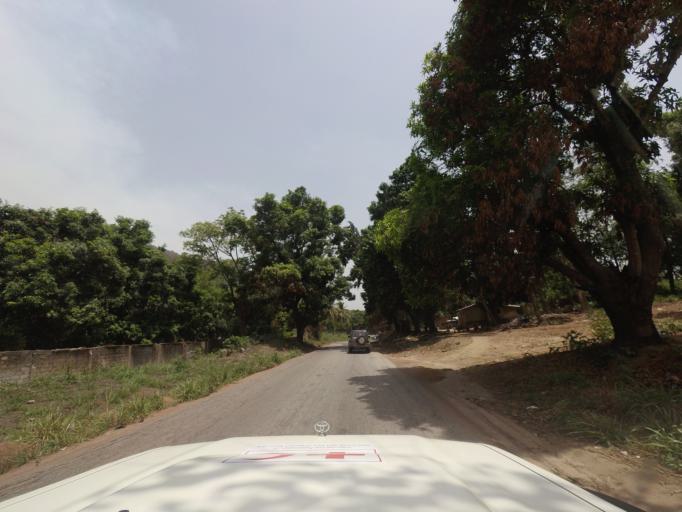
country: GN
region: Kindia
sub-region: Coyah
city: Coyah
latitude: 9.7268
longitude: -13.3707
